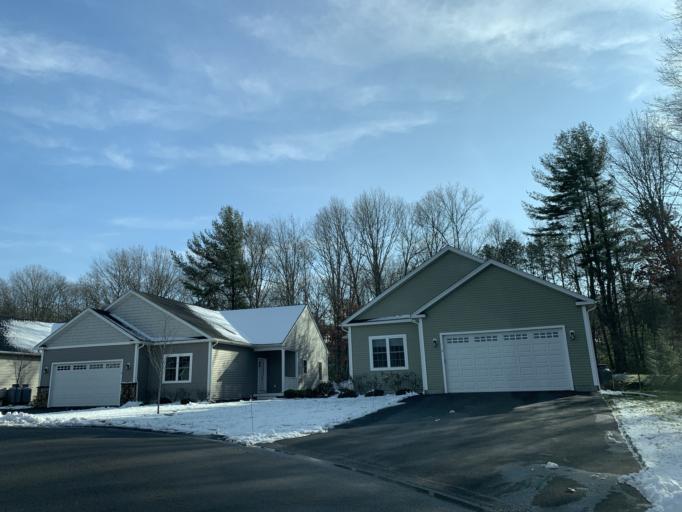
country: US
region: Rhode Island
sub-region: Kent County
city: West Warwick
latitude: 41.6552
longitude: -71.5508
